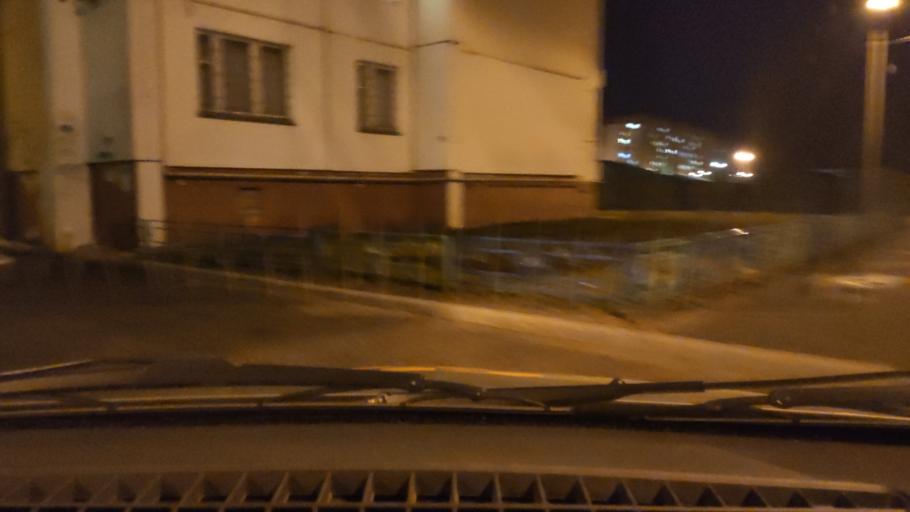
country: RU
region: Voronezj
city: Pridonskoy
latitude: 51.6262
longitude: 39.0769
